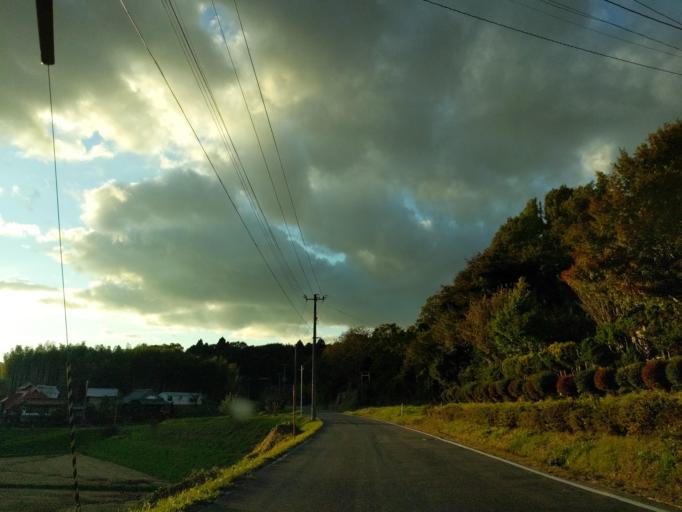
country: JP
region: Fukushima
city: Motomiya
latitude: 37.4763
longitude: 140.4335
